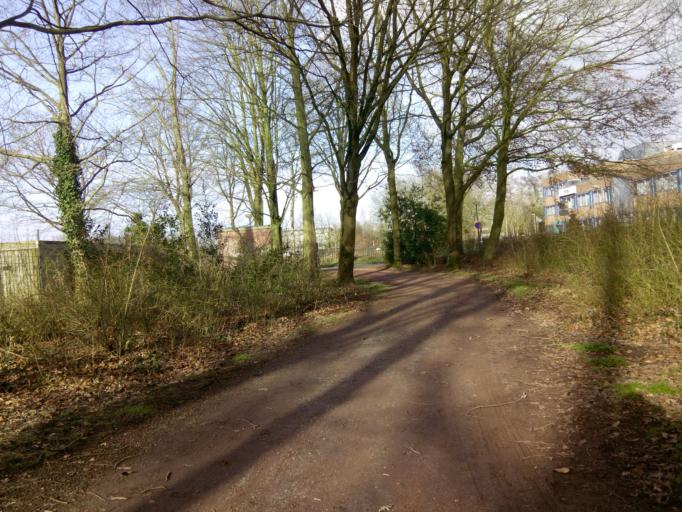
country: NL
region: Utrecht
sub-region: Gemeente Leusden
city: Leusden
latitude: 52.1398
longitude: 5.4223
